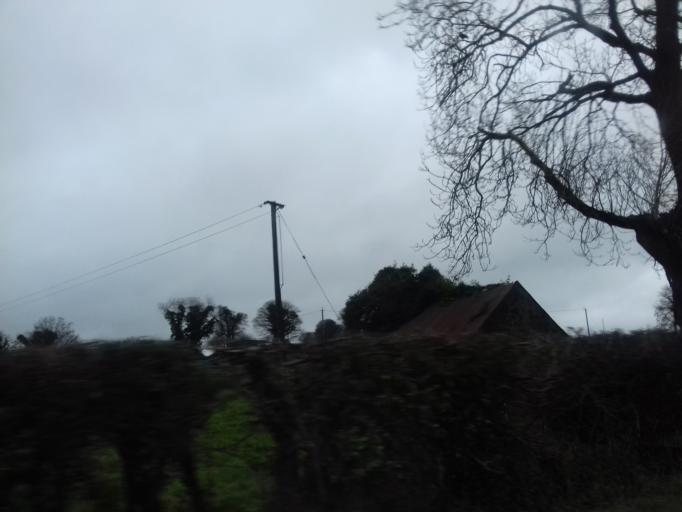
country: IE
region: Ulster
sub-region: County Monaghan
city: Castleblayney
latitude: 54.0707
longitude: -6.6866
